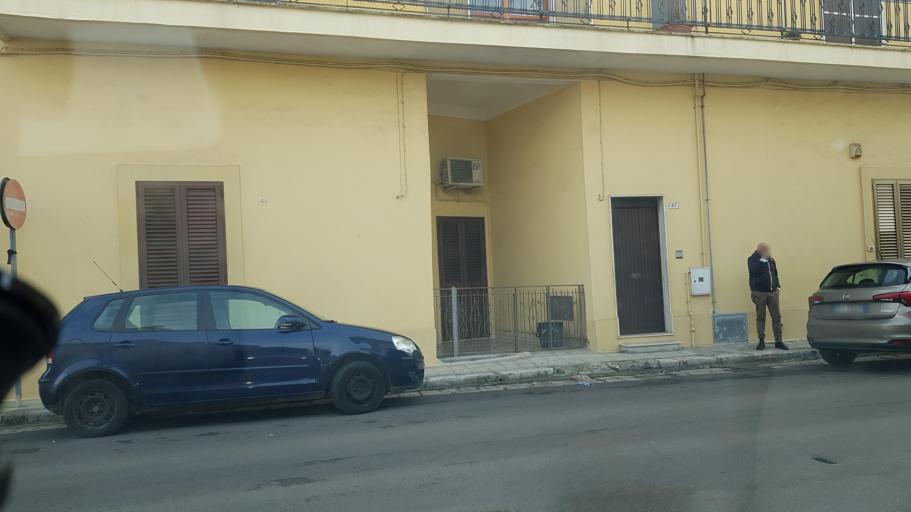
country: IT
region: Apulia
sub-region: Provincia di Lecce
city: Carmiano
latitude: 40.3432
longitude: 18.0429
